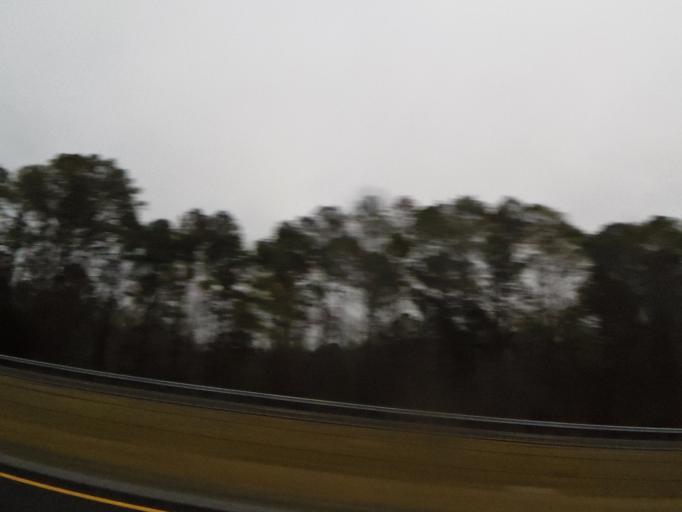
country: US
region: Alabama
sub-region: Cullman County
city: Cullman
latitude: 34.2308
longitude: -86.8791
